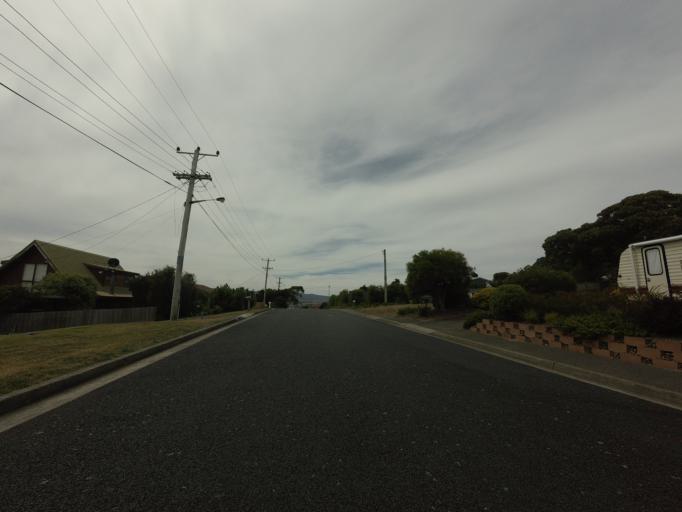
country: AU
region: Tasmania
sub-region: Sorell
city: Sorell
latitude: -42.7951
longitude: 147.5280
